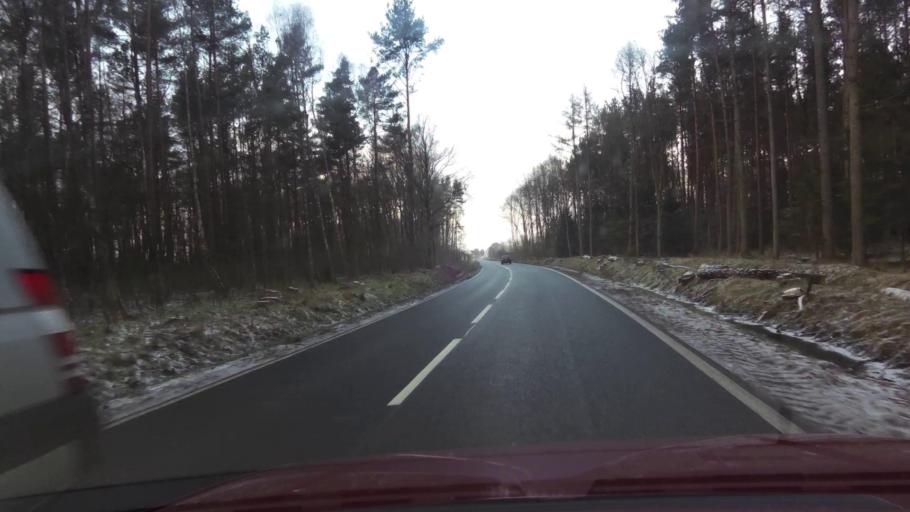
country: PL
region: West Pomeranian Voivodeship
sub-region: Powiat bialogardzki
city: Bialogard
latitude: 54.0683
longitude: 15.9587
